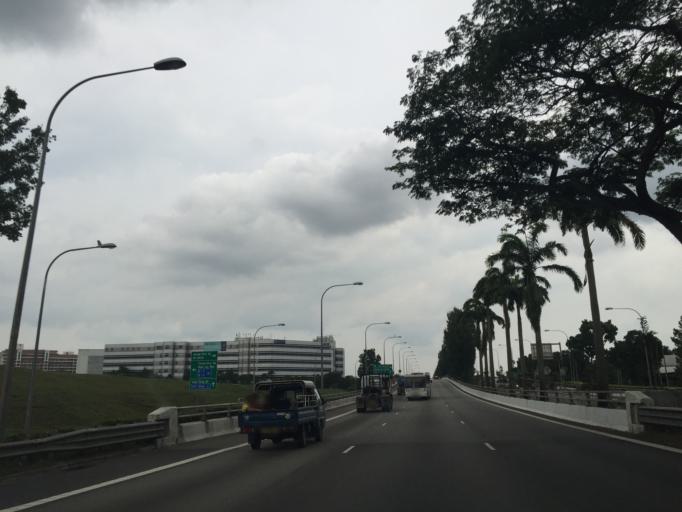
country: SG
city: Singapore
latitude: 1.3230
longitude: 103.7168
